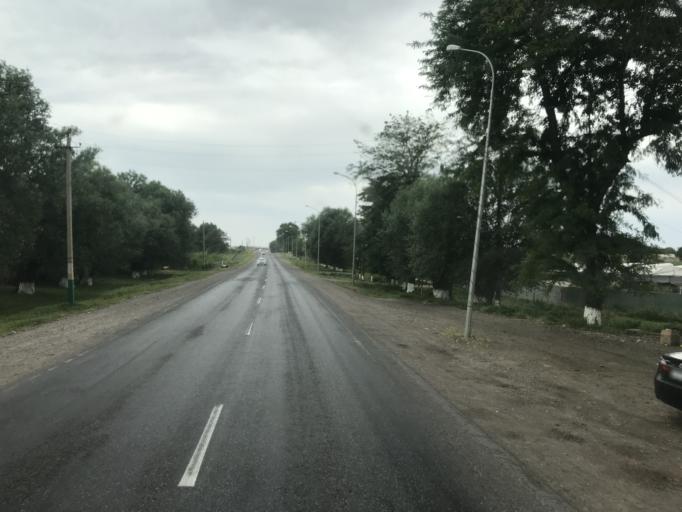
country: KZ
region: Ongtustik Qazaqstan
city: Saryaghash
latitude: 41.4932
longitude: 69.2977
